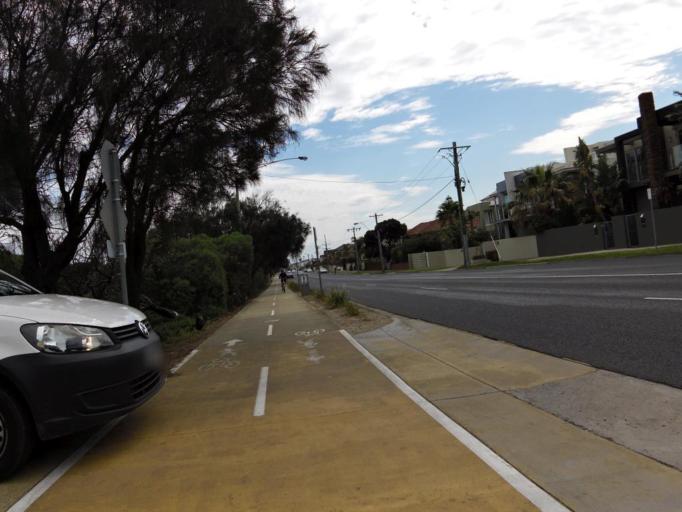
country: AU
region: Victoria
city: Hampton
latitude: -37.9578
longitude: 145.0087
